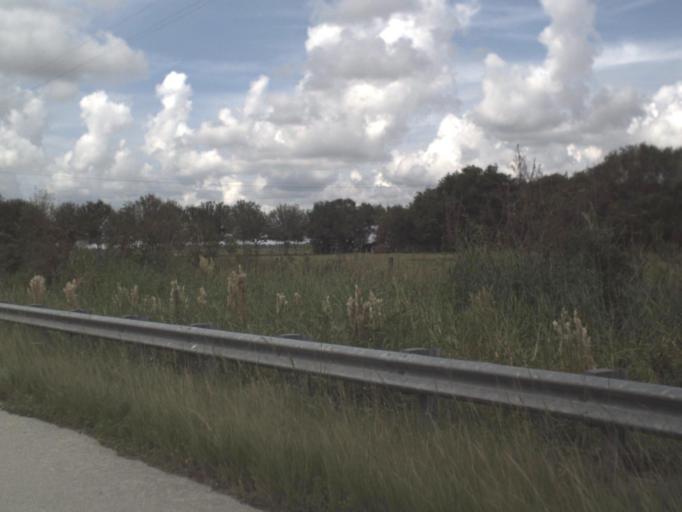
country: US
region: Florida
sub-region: Okeechobee County
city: Okeechobee
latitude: 27.2436
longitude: -80.8992
